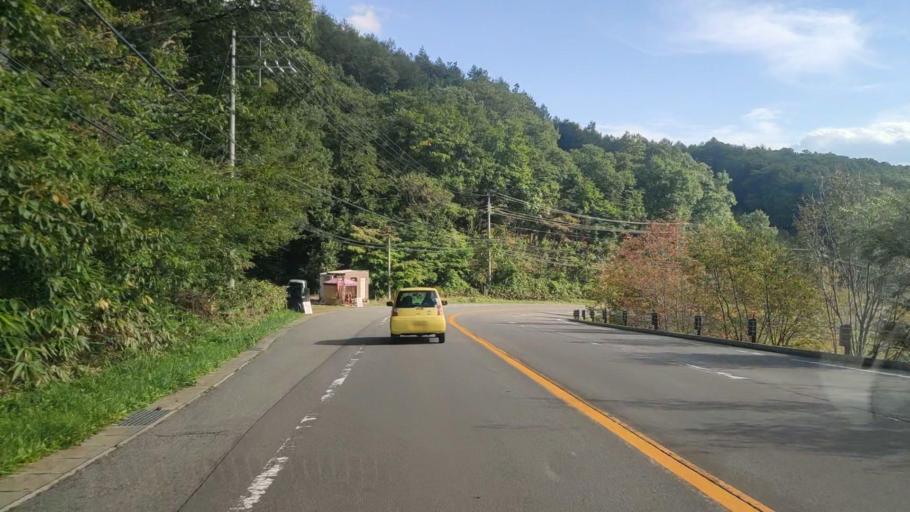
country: JP
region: Gunma
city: Nakanojomachi
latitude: 36.5985
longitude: 138.5869
